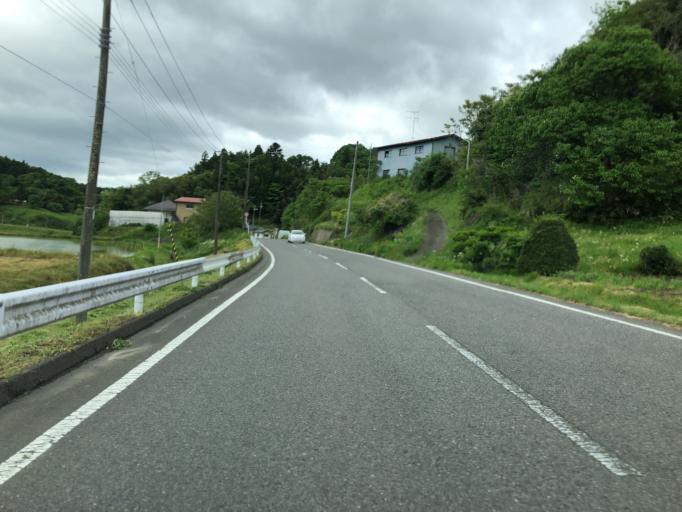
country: JP
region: Fukushima
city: Miharu
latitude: 37.4606
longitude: 140.4750
